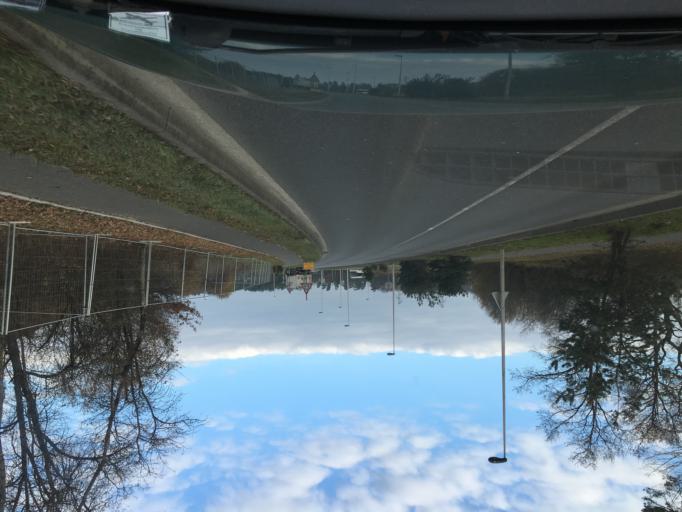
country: FR
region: Centre
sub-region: Departement du Loiret
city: Saran
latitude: 47.9593
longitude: 1.8822
